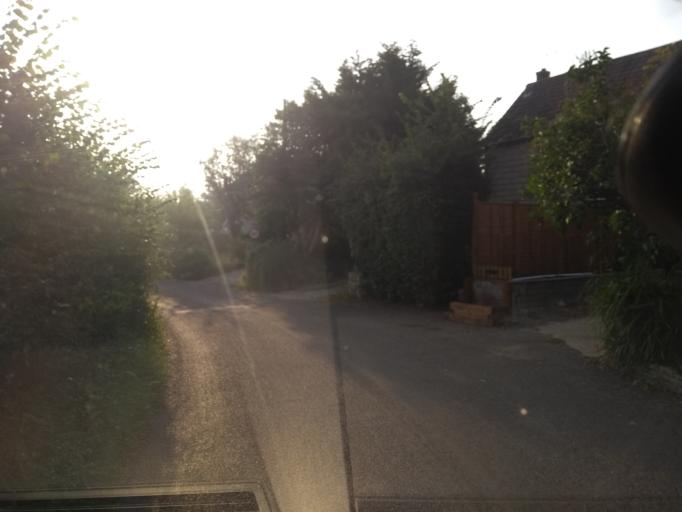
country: GB
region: England
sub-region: Somerset
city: Curry Rivel
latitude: 50.9874
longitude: -2.8670
